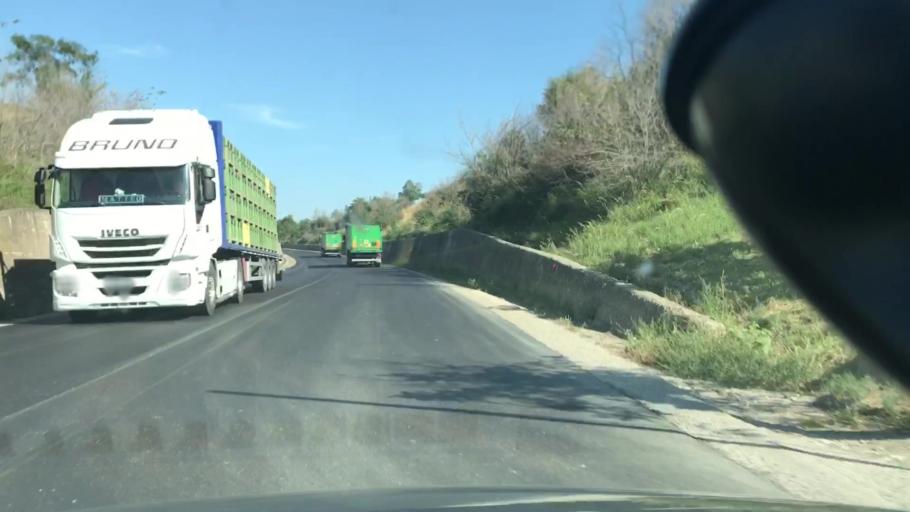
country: IT
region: Apulia
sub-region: Provincia di Foggia
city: Candela
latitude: 41.0991
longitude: 15.5942
